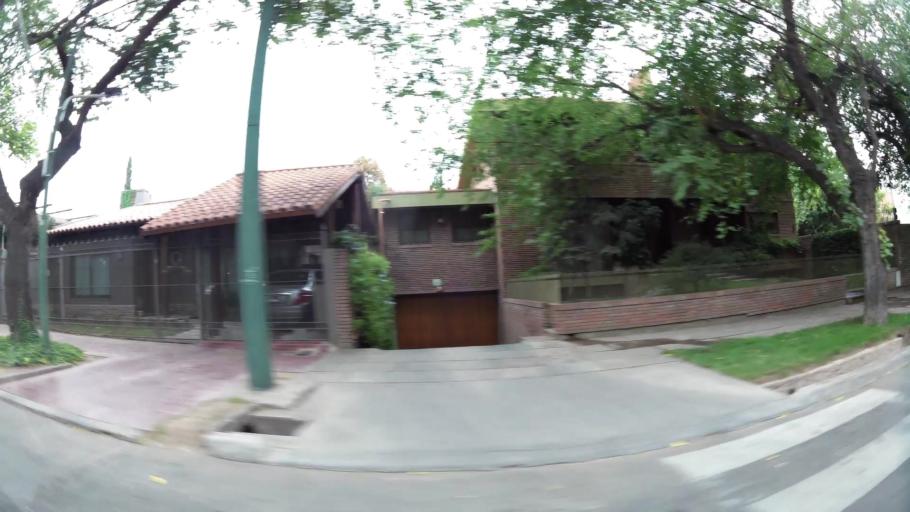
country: AR
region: Mendoza
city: Mendoza
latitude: -32.8888
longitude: -68.8613
